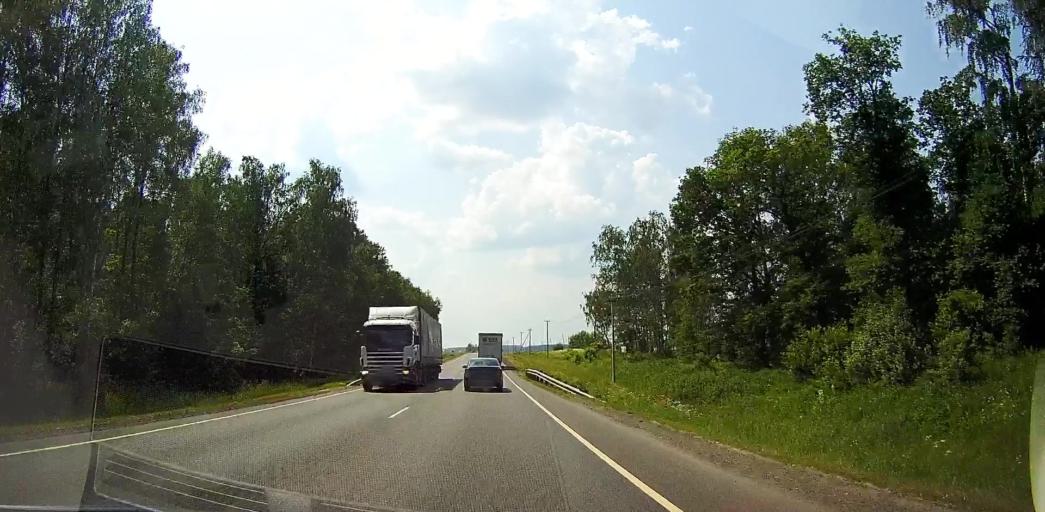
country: RU
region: Moskovskaya
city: Malino
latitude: 55.1369
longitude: 38.2676
